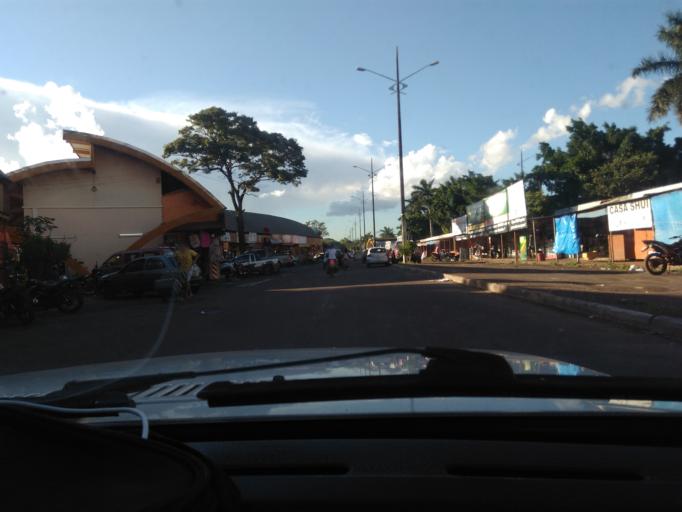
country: BR
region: Mato Grosso do Sul
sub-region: Ponta Pora
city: Ponta Pora
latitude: -22.5404
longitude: -55.7301
